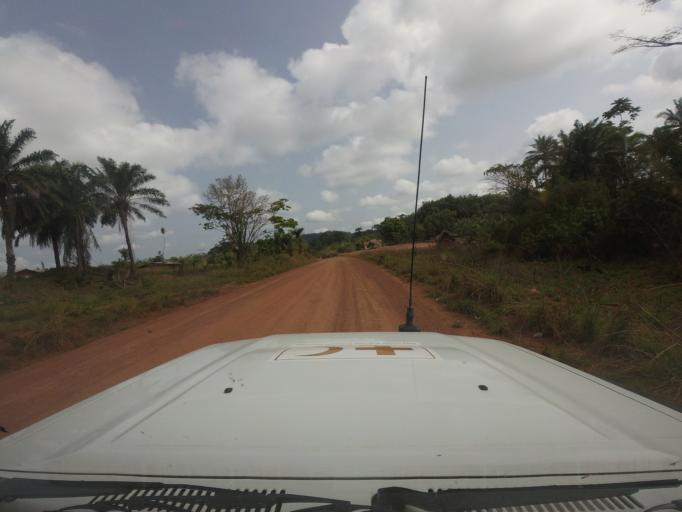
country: LR
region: Bong
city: Gbarnga
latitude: 7.2362
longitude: -9.4375
